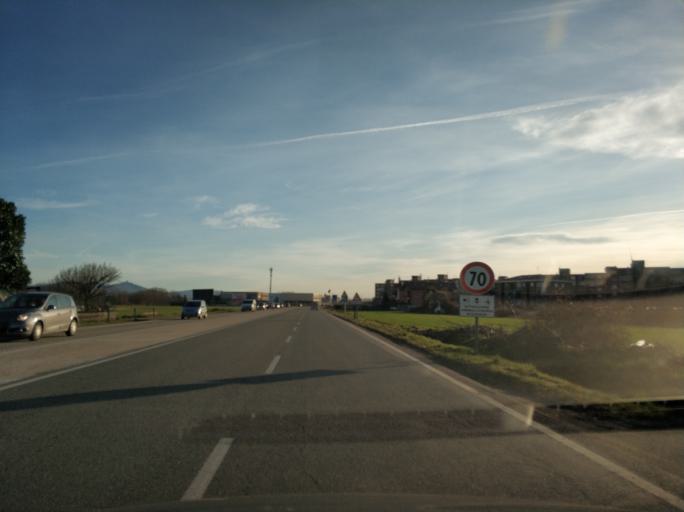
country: IT
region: Piedmont
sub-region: Provincia di Torino
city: Volpiano
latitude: 45.1949
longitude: 7.7881
